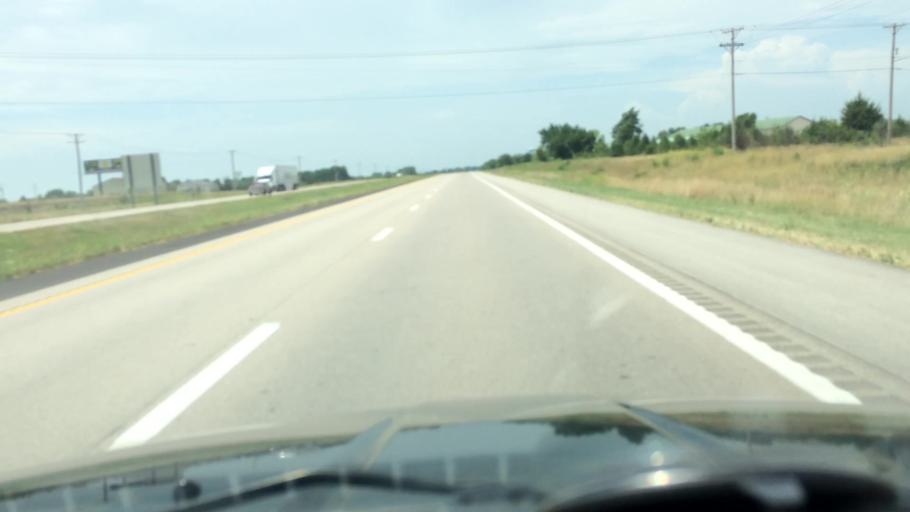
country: US
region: Missouri
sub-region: Polk County
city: Bolivar
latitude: 37.5852
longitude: -93.4171
